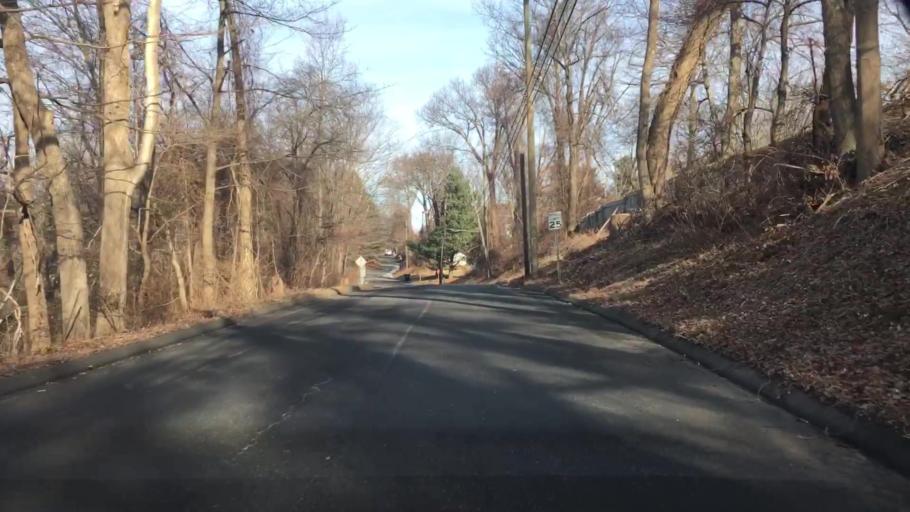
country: US
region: Connecticut
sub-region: Fairfield County
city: Danbury
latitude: 41.3712
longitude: -73.5043
